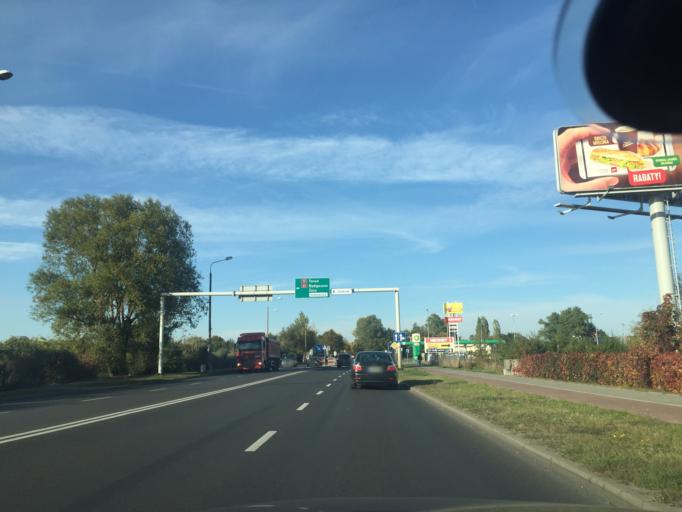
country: PL
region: Kujawsko-Pomorskie
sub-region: Powiat inowroclawski
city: Inowroclaw
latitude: 52.7859
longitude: 18.2608
